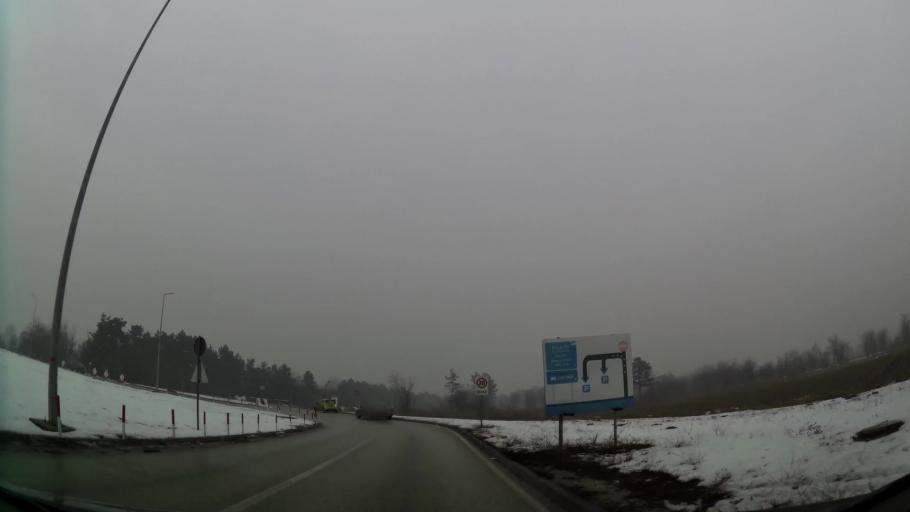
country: MK
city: Miladinovci
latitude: 41.9629
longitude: 21.6293
